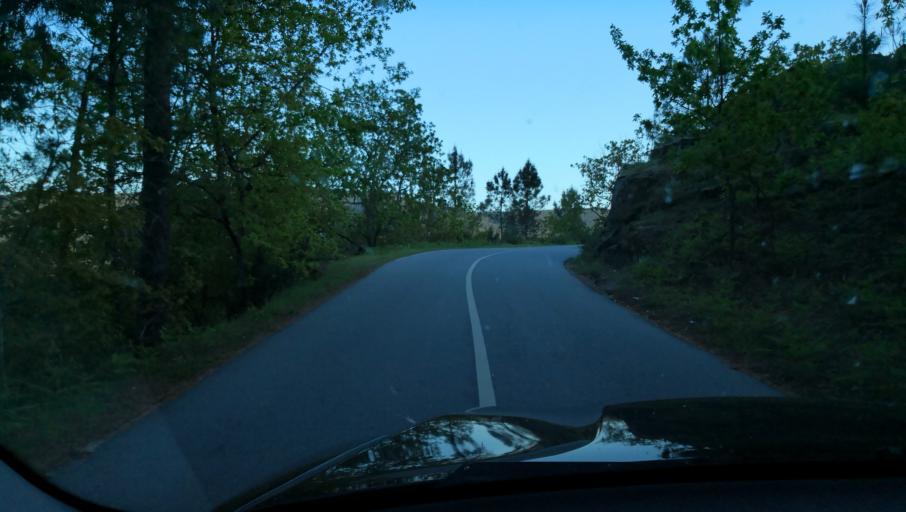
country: PT
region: Vila Real
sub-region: Mondim de Basto
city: Mondim de Basto
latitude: 41.4062
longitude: -7.9150
